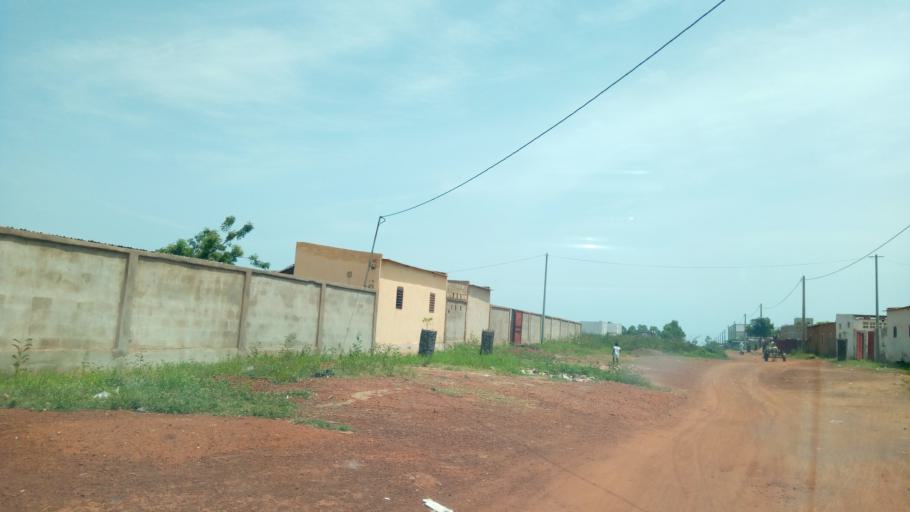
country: ML
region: Sikasso
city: Koutiala
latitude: 12.4144
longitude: -5.4723
